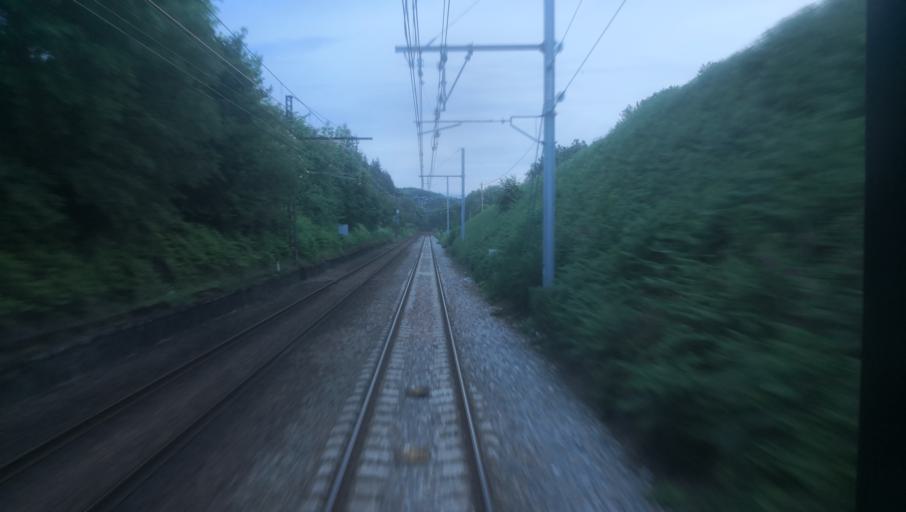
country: FR
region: Limousin
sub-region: Departement de la Haute-Vienne
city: Bessines-sur-Gartempe
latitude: 46.0533
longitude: 1.4658
